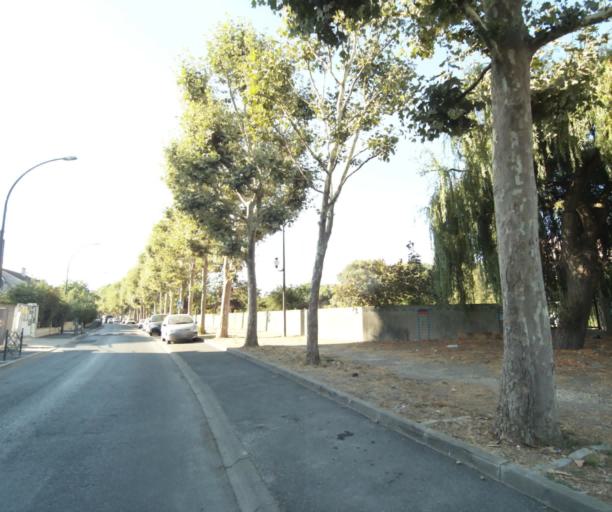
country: FR
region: Ile-de-France
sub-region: Departement de Seine-Saint-Denis
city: Villetaneuse
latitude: 48.9407
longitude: 2.3347
